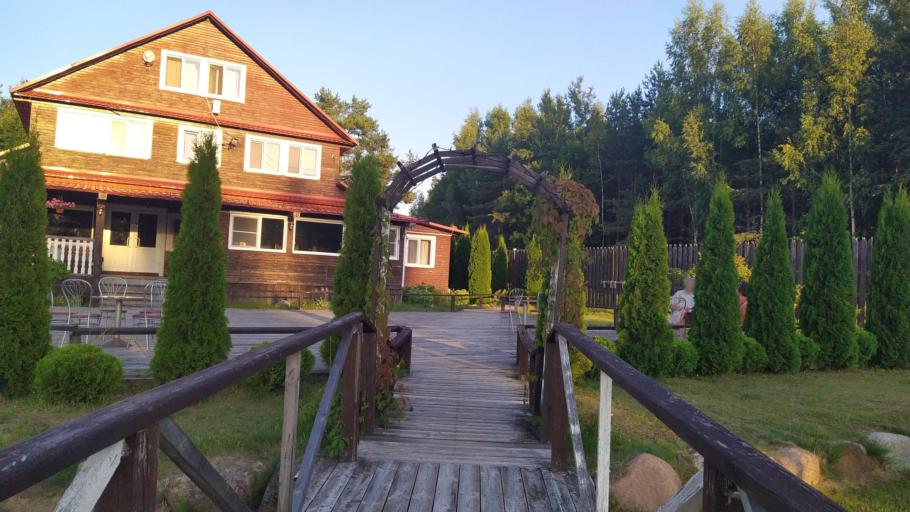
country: RU
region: Pskov
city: Pushkinskiye Gory
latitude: 56.9824
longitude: 29.0038
